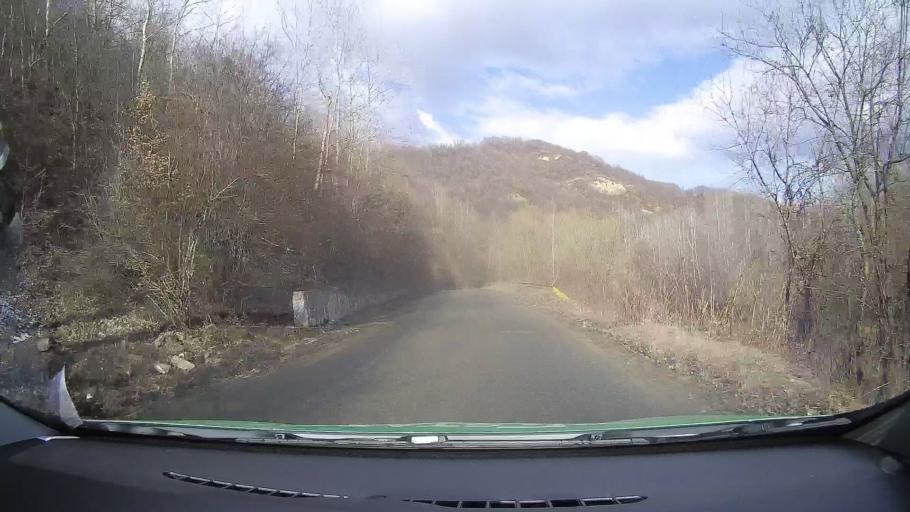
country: RO
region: Dambovita
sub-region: Oras Pucioasa
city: Pucioasa
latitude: 45.1005
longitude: 25.4418
